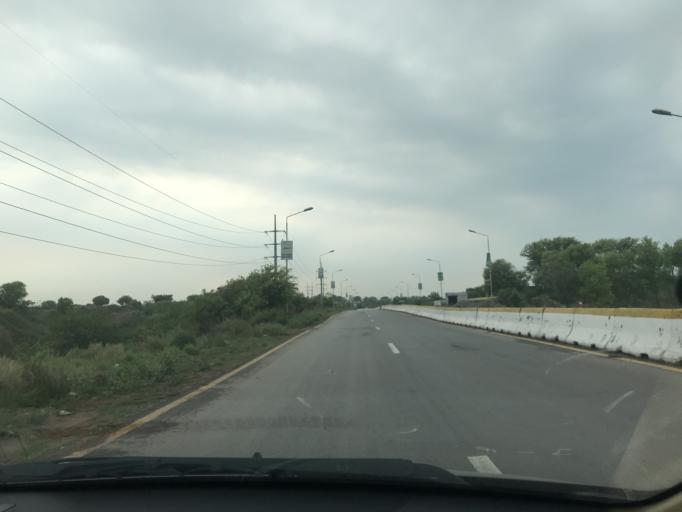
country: PK
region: Islamabad
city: Islamabad
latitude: 33.6965
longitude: 73.1791
